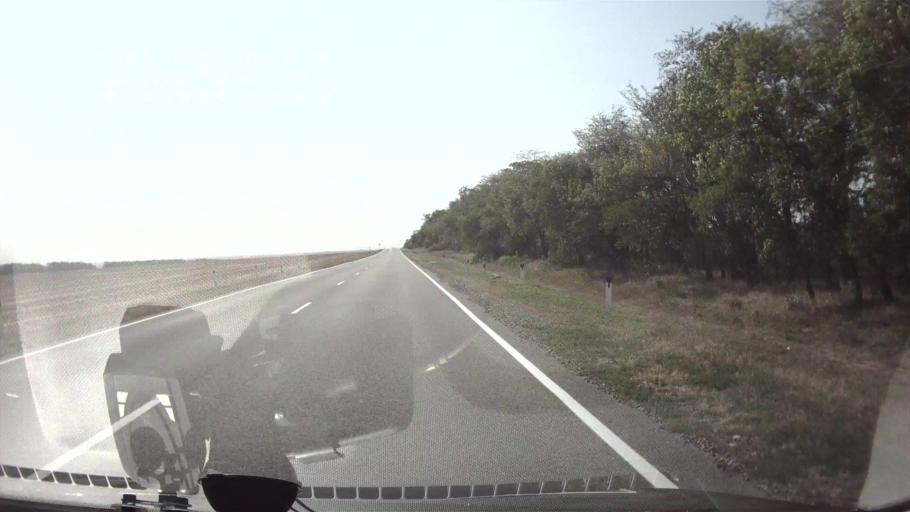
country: RU
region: Krasnodarskiy
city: Dmitriyevskaya
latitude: 45.7779
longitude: 40.7198
